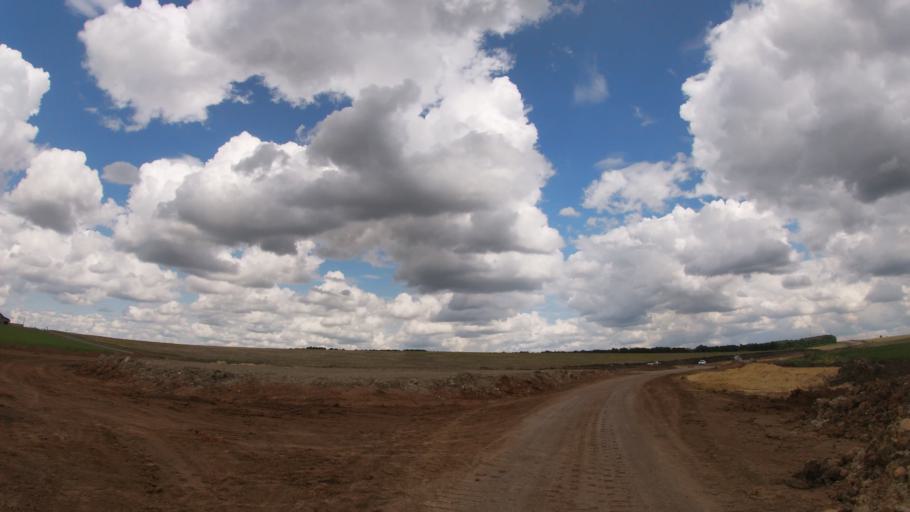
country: RU
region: Belgorod
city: Mayskiy
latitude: 50.5179
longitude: 36.4923
